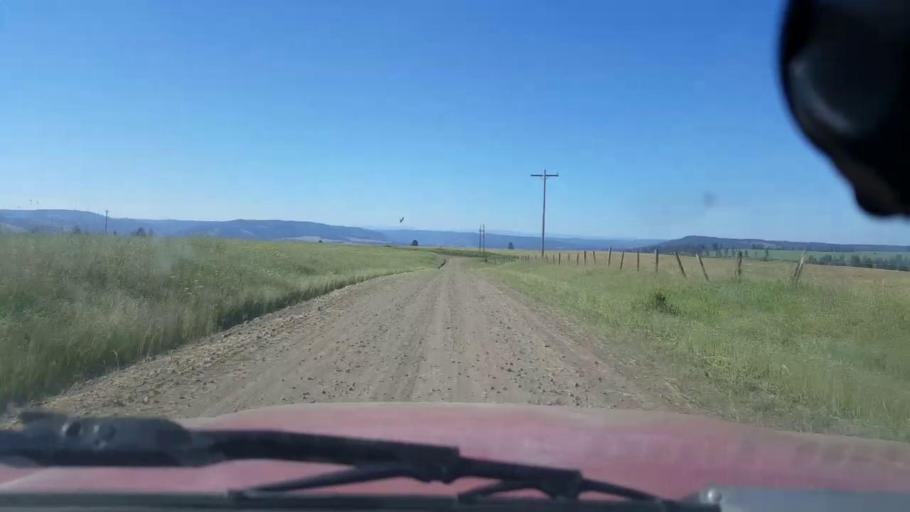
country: US
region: Washington
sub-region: Garfield County
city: Pomeroy
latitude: 45.9865
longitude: -117.4580
